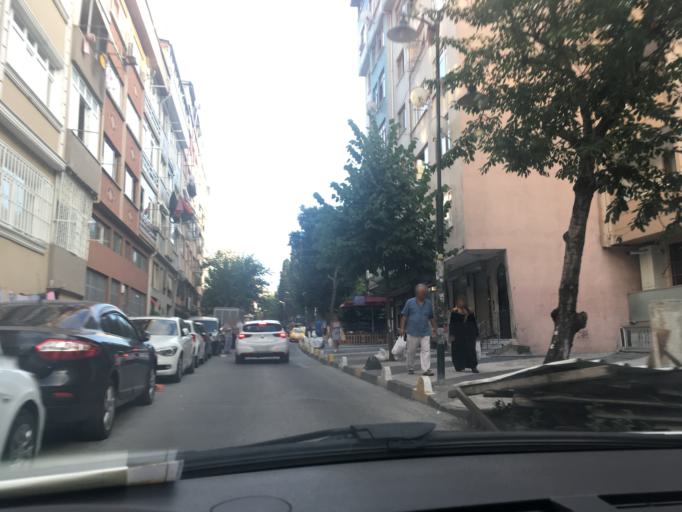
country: TR
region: Istanbul
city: Sisli
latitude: 41.0531
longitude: 28.9748
